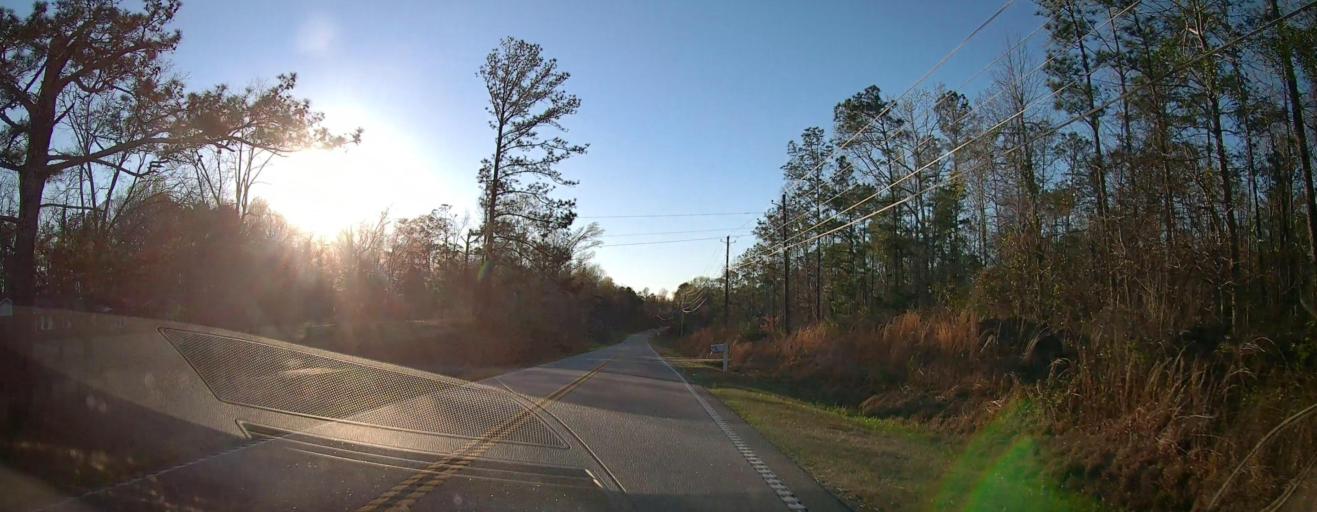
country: US
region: Georgia
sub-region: Harris County
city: Hamilton
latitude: 32.6284
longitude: -84.7930
